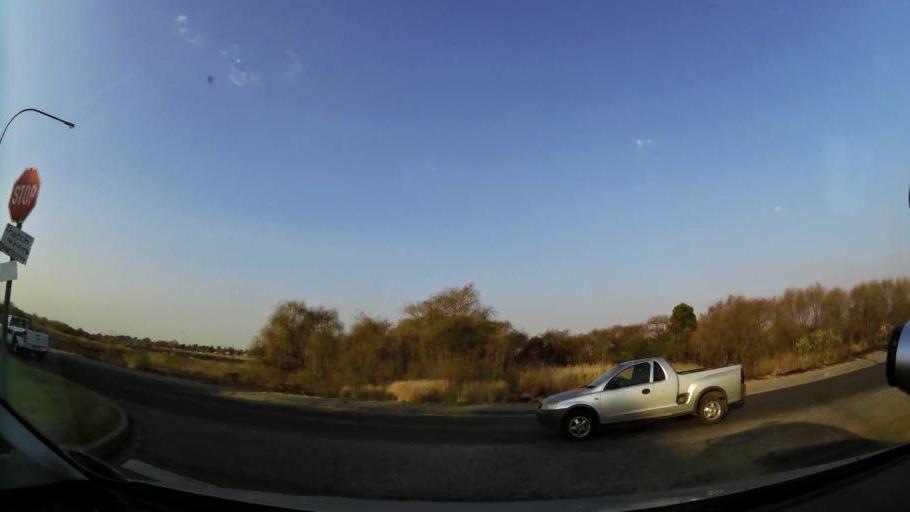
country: ZA
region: Gauteng
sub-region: City of Johannesburg Metropolitan Municipality
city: Modderfontein
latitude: -26.0866
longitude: 28.2185
